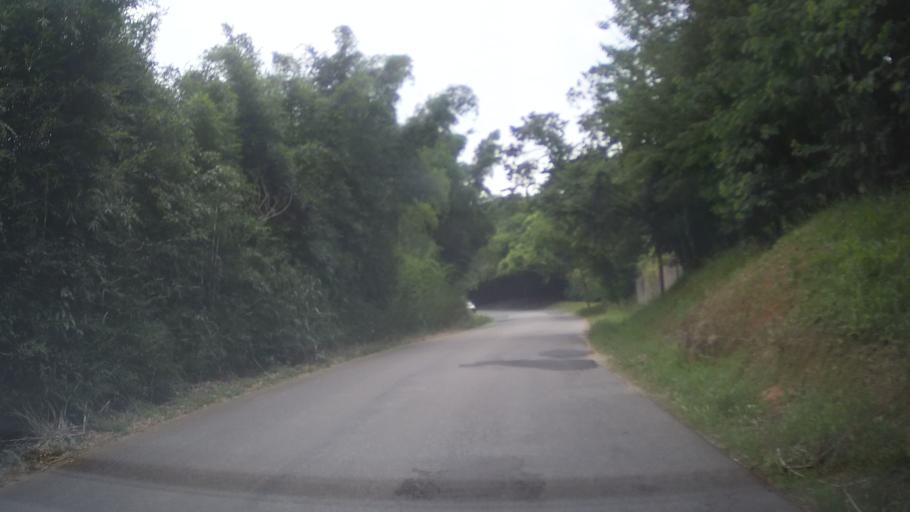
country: BR
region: Sao Paulo
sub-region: Itupeva
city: Itupeva
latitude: -23.1687
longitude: -47.1071
